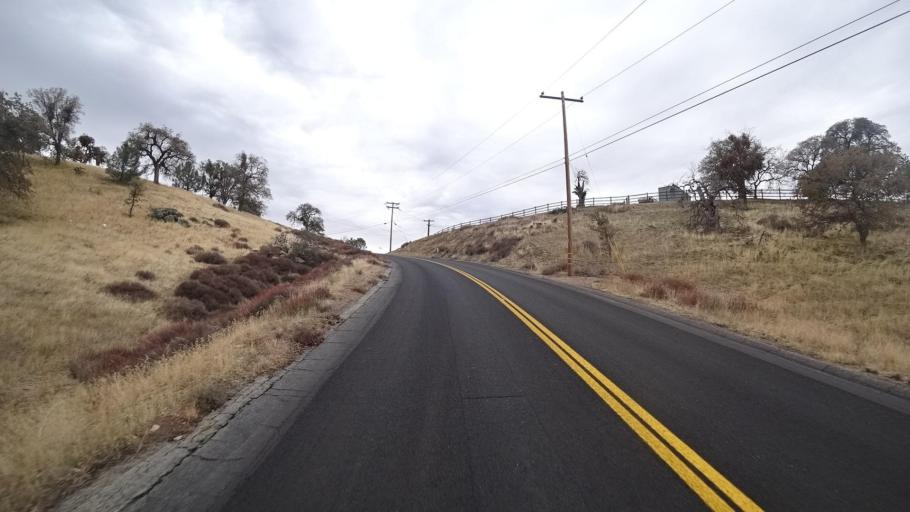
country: US
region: California
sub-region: Kern County
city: Stallion Springs
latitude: 35.0998
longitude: -118.6705
